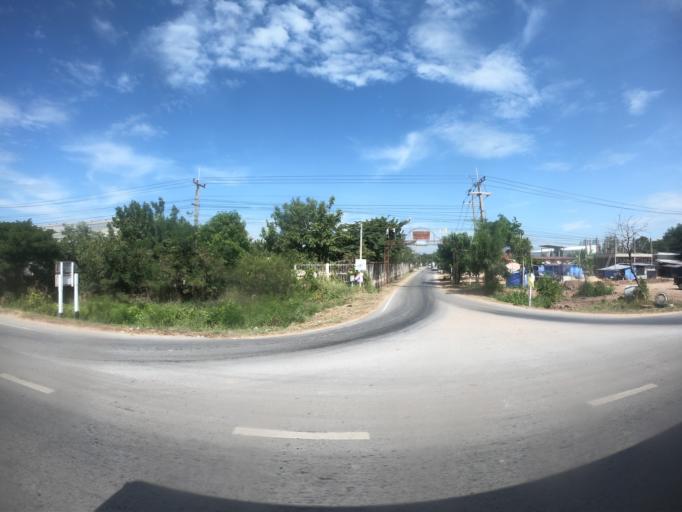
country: TH
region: Khon Kaen
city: Khon Kaen
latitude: 16.4109
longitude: 102.9000
